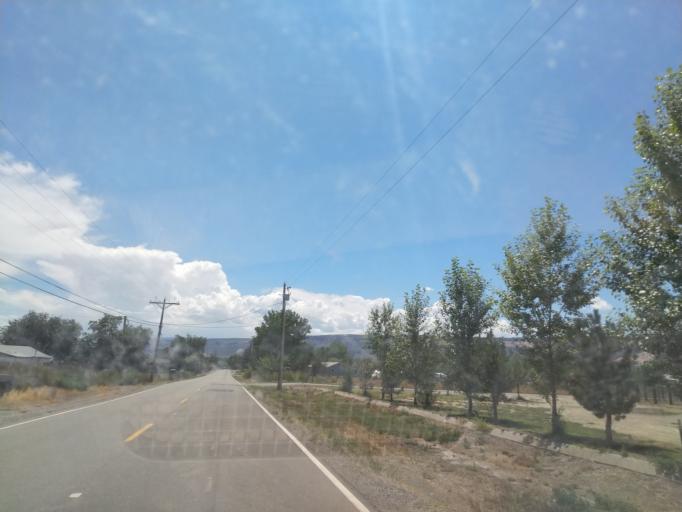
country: US
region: Colorado
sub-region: Mesa County
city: Redlands
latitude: 39.1288
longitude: -108.6640
